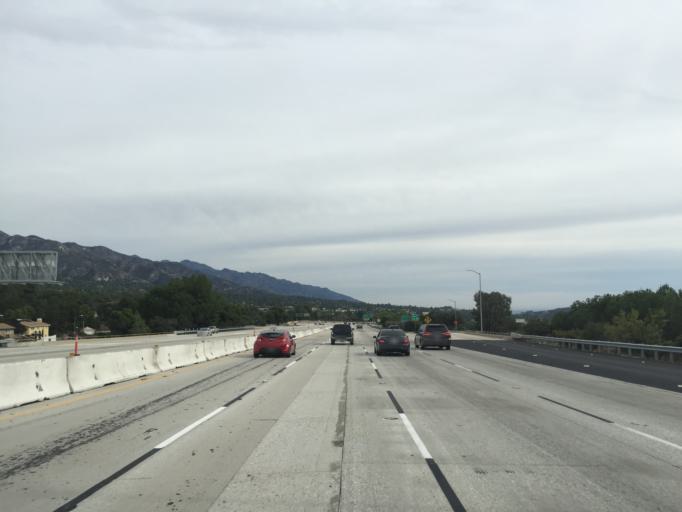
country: US
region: California
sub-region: Los Angeles County
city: La Crescenta-Montrose
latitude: 34.2314
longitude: -118.2676
